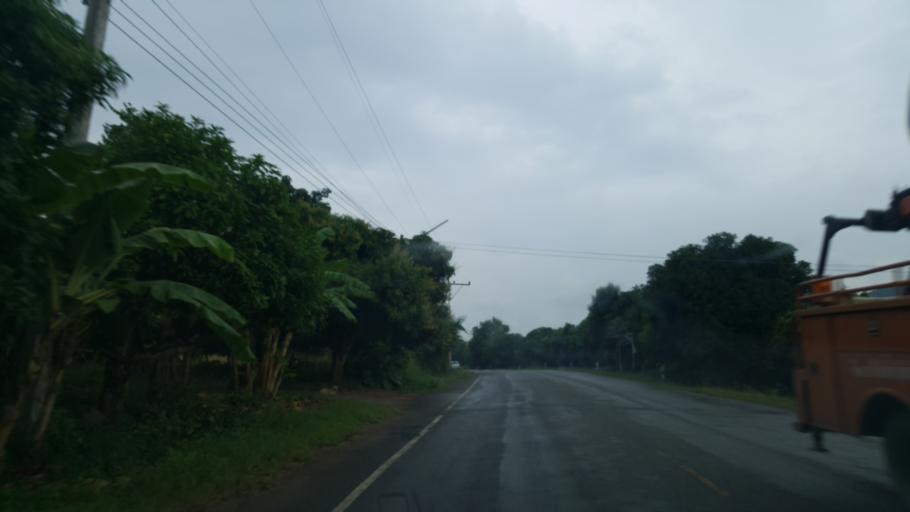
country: TH
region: Chon Buri
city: Sattahip
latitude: 12.7170
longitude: 100.9192
